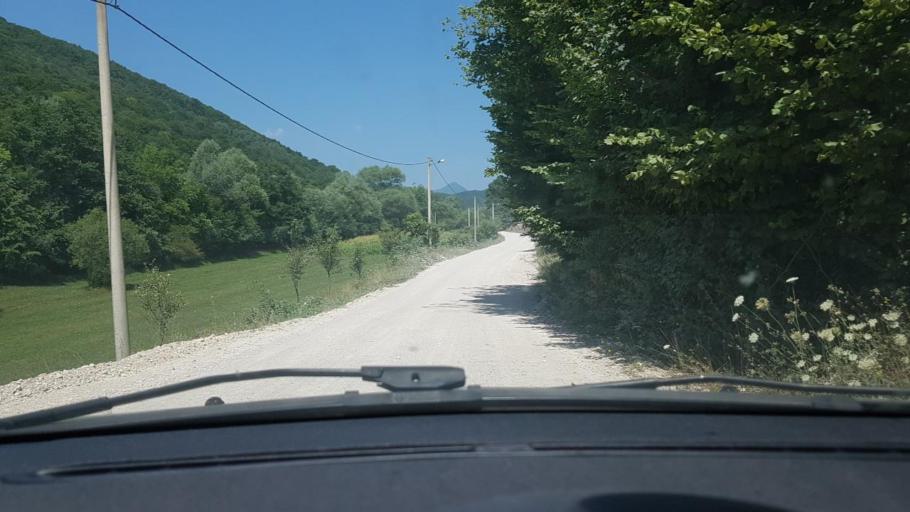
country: BA
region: Federation of Bosnia and Herzegovina
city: Orasac
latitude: 44.5402
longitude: 16.1104
